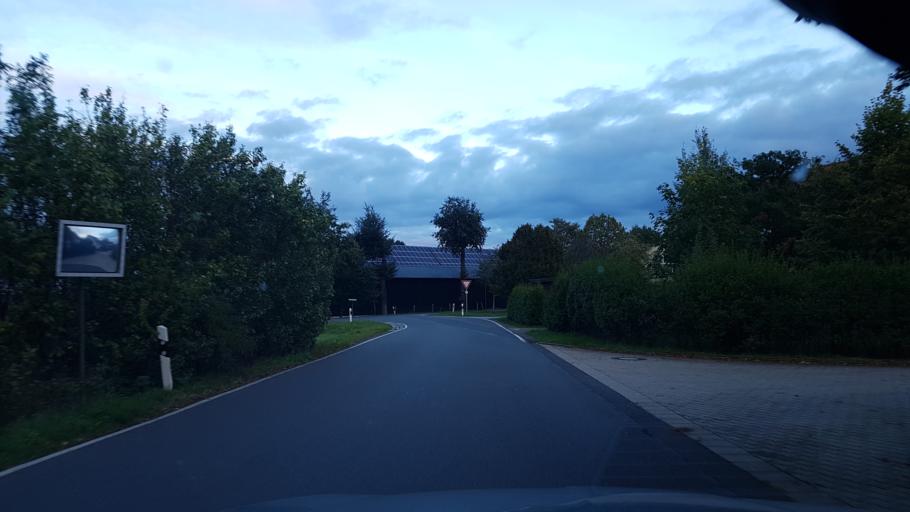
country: DE
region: Saxony
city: Ebersbach
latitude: 51.2791
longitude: 13.6228
